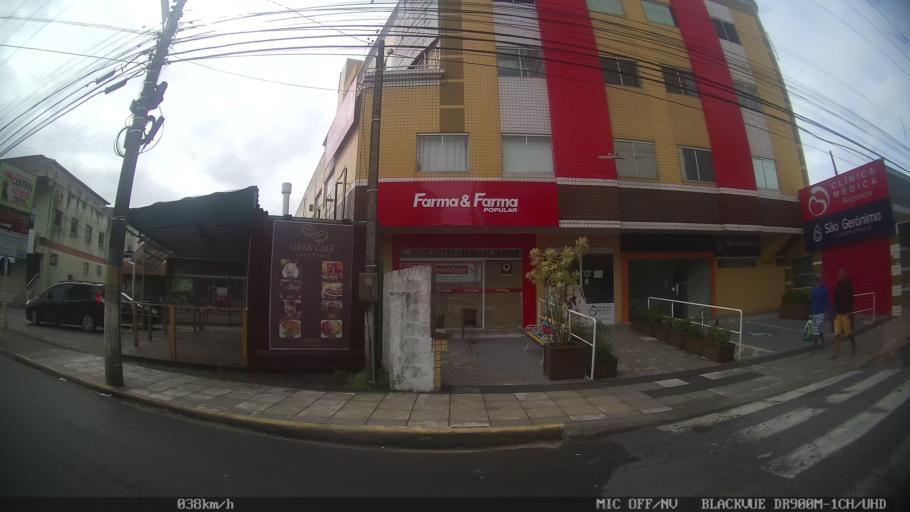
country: BR
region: Santa Catarina
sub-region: Biguacu
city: Biguacu
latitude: -27.4988
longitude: -48.6548
